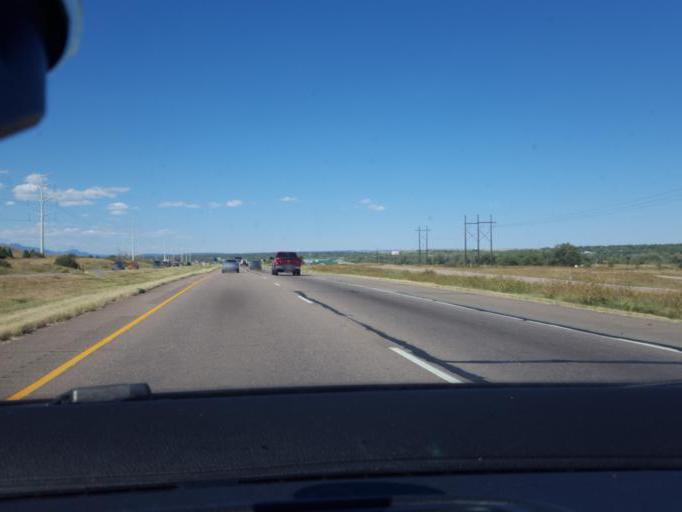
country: US
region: Colorado
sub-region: El Paso County
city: Fountain
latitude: 38.6966
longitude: -104.7209
